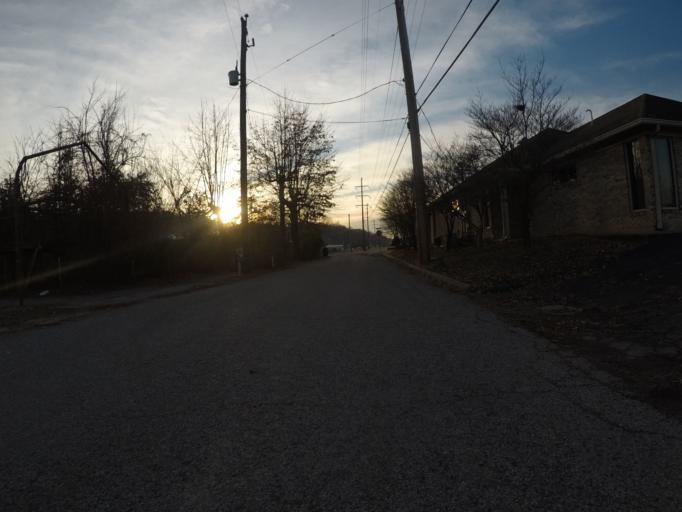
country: US
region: Ohio
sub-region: Lawrence County
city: Burlington
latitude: 38.3991
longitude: -82.5159
